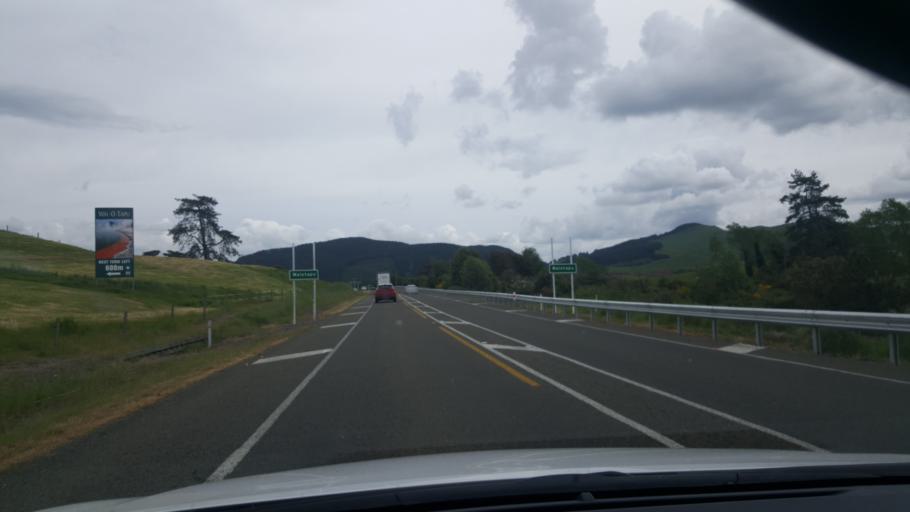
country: NZ
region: Bay of Plenty
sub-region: Rotorua District
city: Rotorua
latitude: -38.3346
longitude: 176.3667
